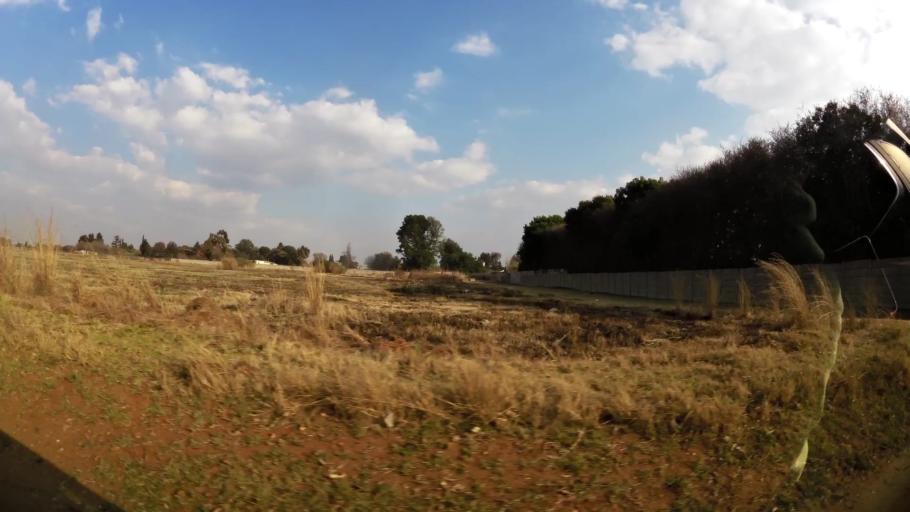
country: ZA
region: Gauteng
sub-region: Ekurhuleni Metropolitan Municipality
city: Benoni
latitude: -26.1011
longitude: 28.2785
